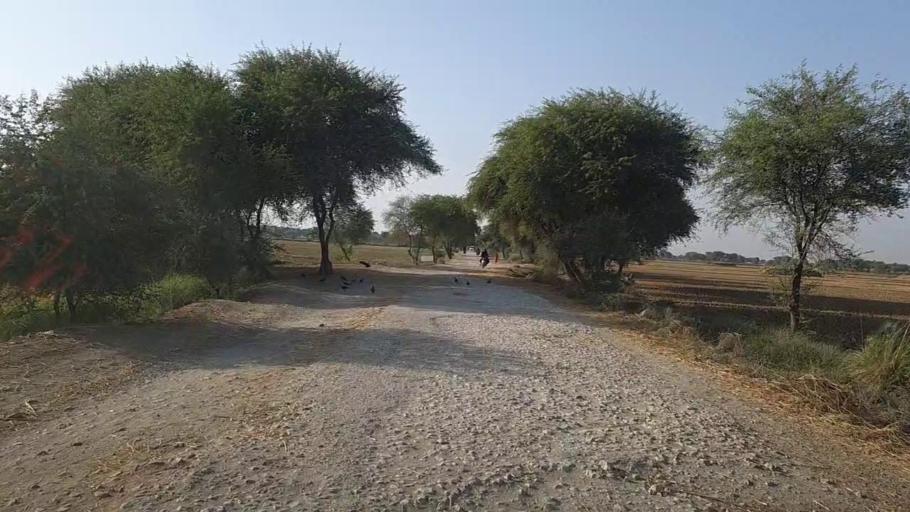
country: PK
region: Sindh
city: Kashmor
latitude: 28.4031
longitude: 69.4178
